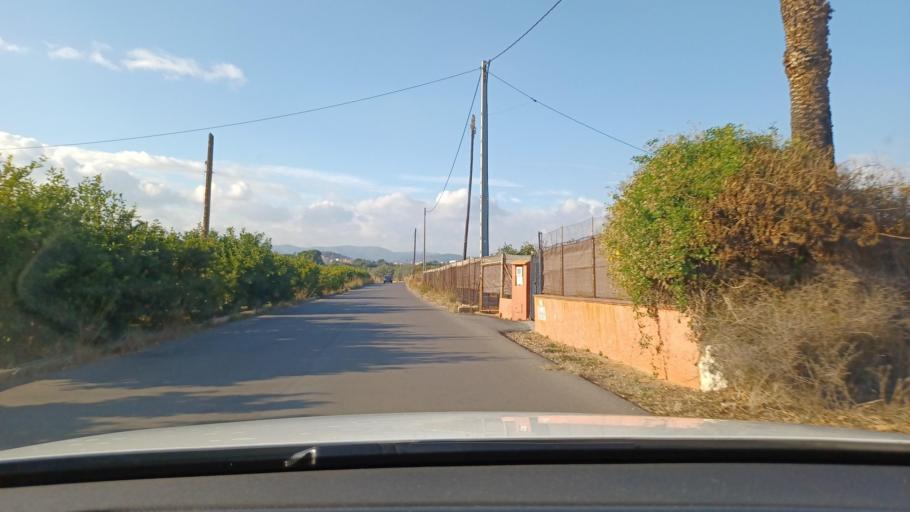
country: ES
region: Valencia
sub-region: Provincia de Castello
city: Onda
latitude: 39.9524
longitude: -0.2310
